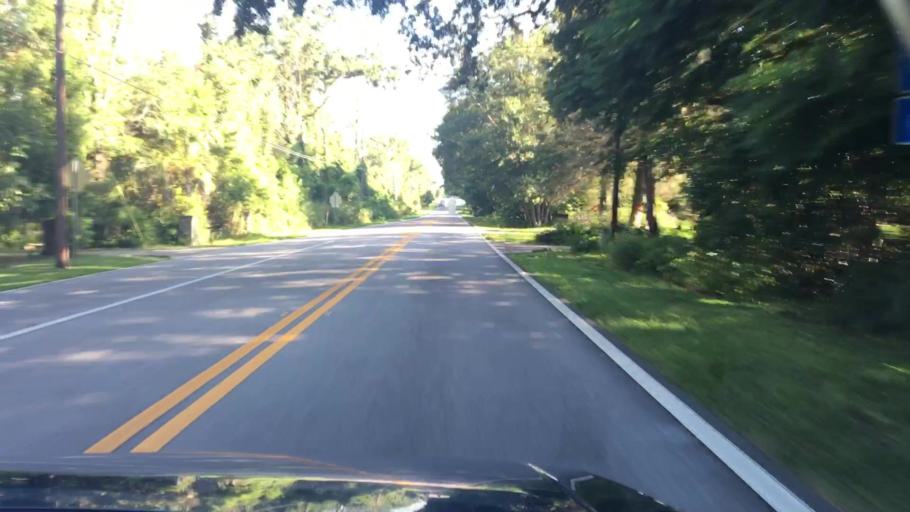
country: US
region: Florida
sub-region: Lake County
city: Eustis
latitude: 28.8591
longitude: -81.6529
